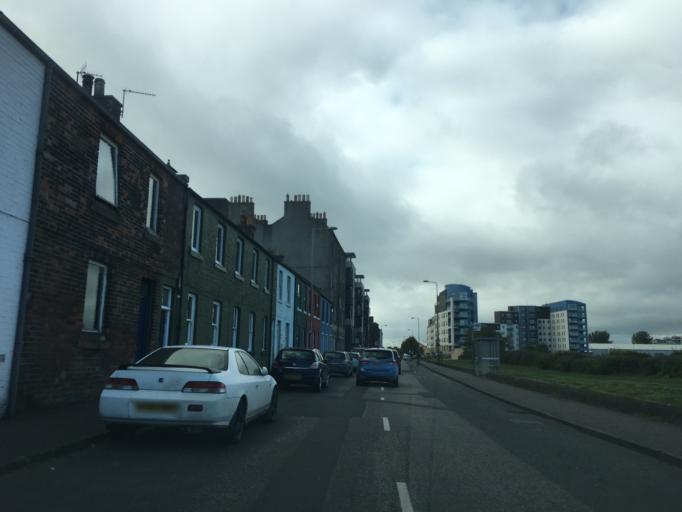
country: GB
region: Scotland
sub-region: Edinburgh
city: Edinburgh
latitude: 55.9800
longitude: -3.2193
